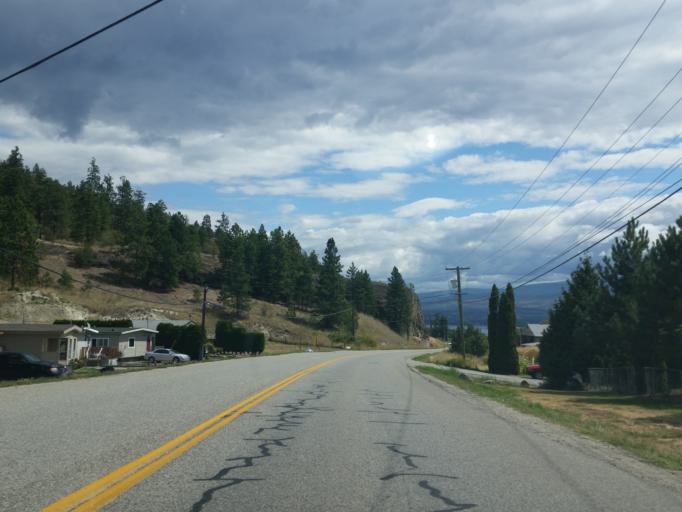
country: CA
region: British Columbia
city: West Kelowna
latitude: 49.8316
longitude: -119.5931
